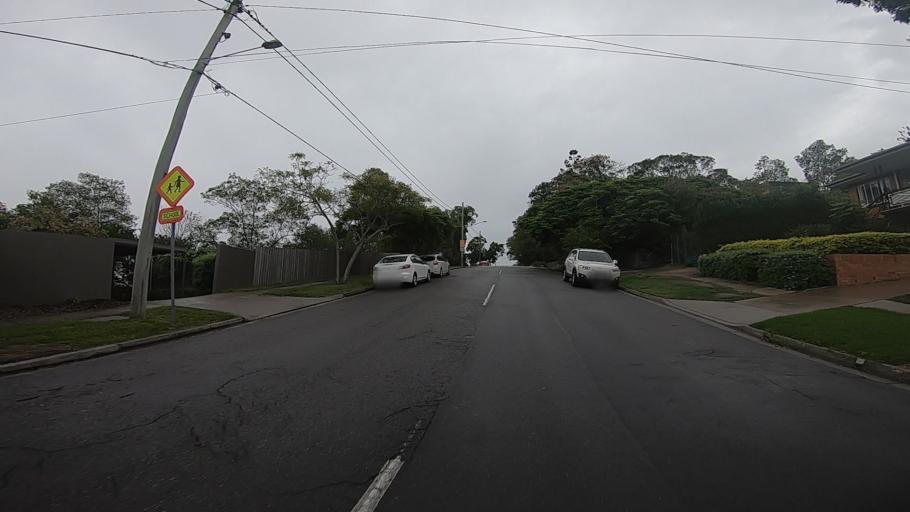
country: AU
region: Queensland
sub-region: Brisbane
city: Ascot
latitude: -27.4314
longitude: 153.0482
